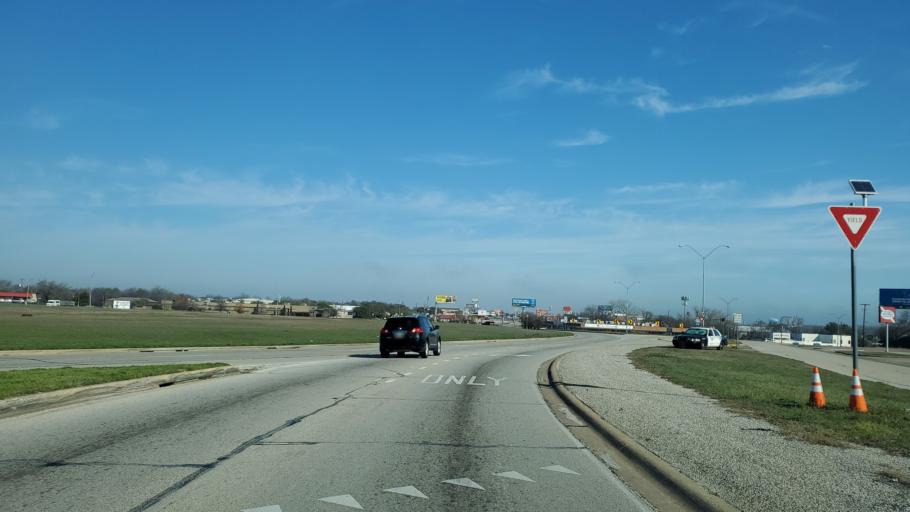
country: US
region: Texas
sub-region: Tarrant County
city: White Settlement
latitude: 32.7160
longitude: -97.4425
